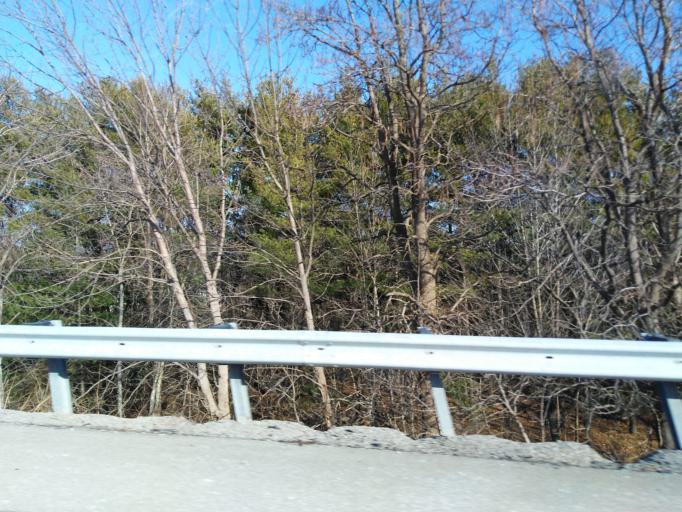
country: US
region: Illinois
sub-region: Franklin County
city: Benton
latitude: 37.9809
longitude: -88.9353
